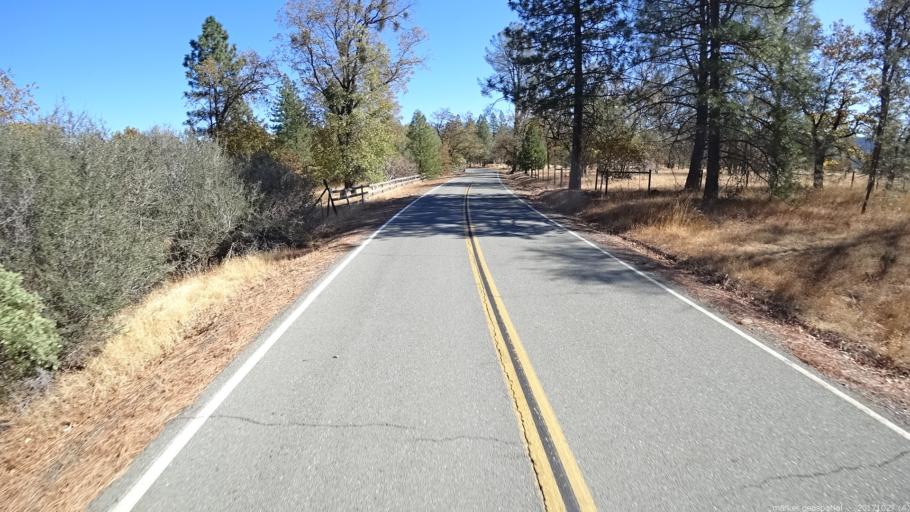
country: US
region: California
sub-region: Shasta County
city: Shingletown
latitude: 40.7526
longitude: -121.9802
